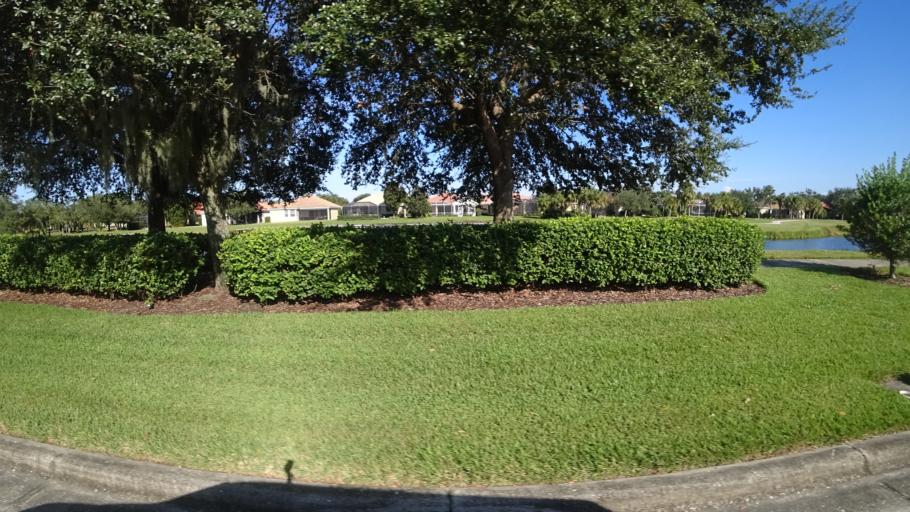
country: US
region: Florida
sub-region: Sarasota County
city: Desoto Lakes
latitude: 27.4270
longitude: -82.4677
